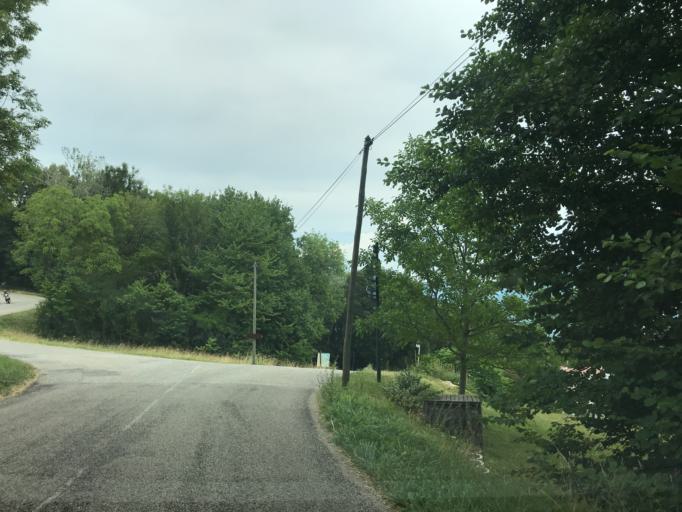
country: FR
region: Rhone-Alpes
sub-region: Departement de l'Isere
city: Chapareillan
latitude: 45.4767
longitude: 5.9662
